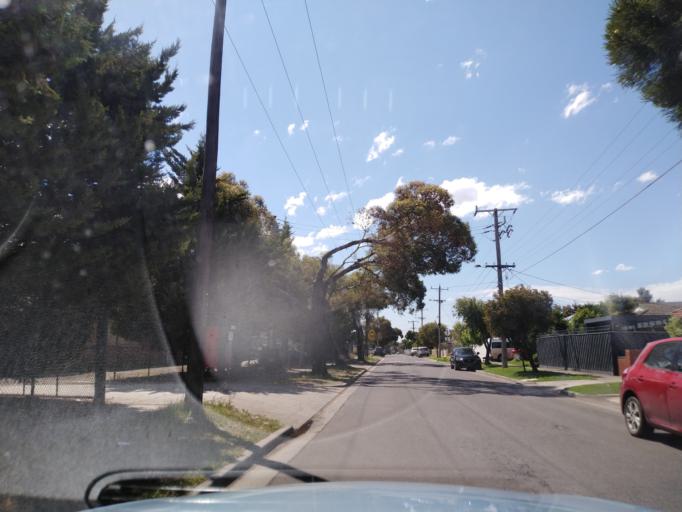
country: AU
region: Victoria
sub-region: Hobsons Bay
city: South Kingsville
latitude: -37.8322
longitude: 144.8663
